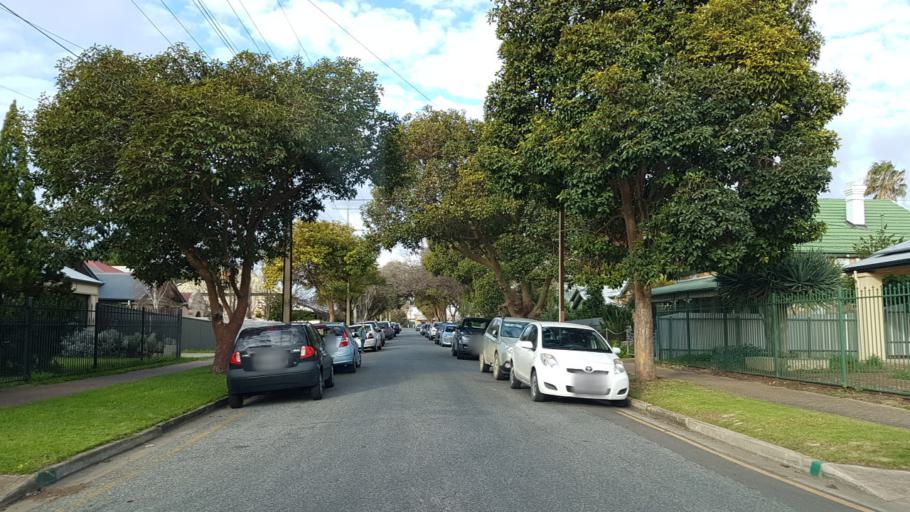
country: AU
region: South Australia
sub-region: Prospect
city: Prospect
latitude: -34.8880
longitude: 138.5996
